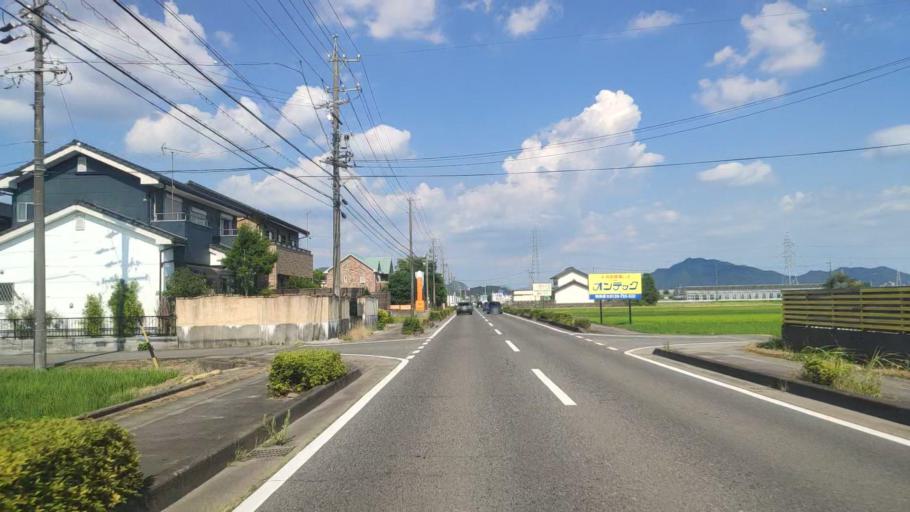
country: JP
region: Gifu
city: Gifu-shi
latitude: 35.4505
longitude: 136.7179
